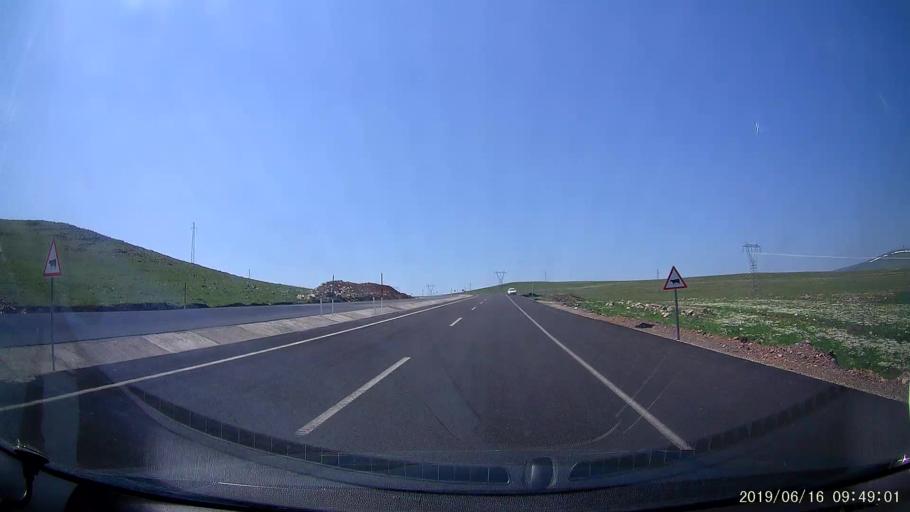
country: TR
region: Kars
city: Digor
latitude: 40.4263
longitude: 43.3563
